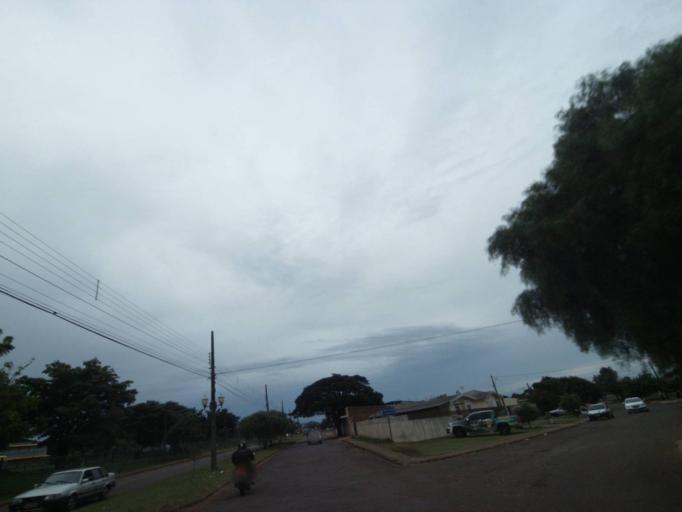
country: BR
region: Parana
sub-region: Campo Mourao
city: Campo Mourao
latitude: -24.0229
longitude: -52.3560
